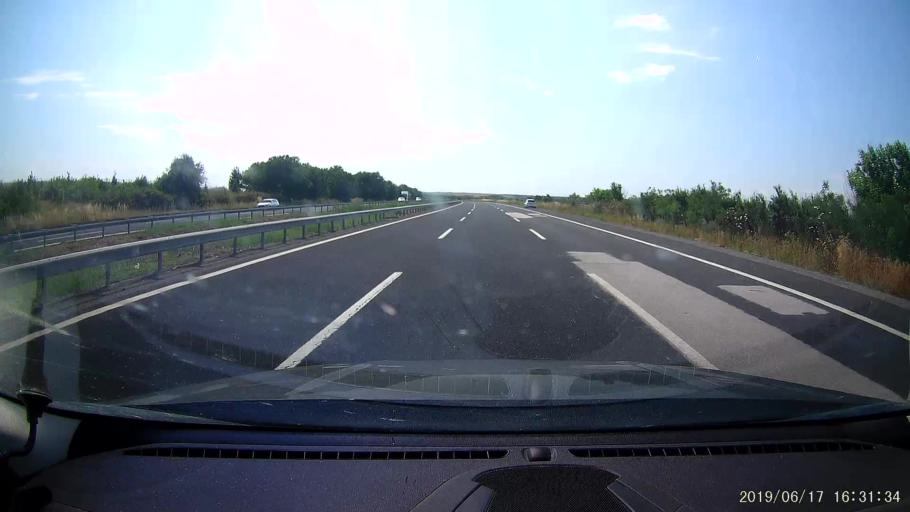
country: TR
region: Tekirdag
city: Beyazkoy
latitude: 41.3627
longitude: 27.6241
